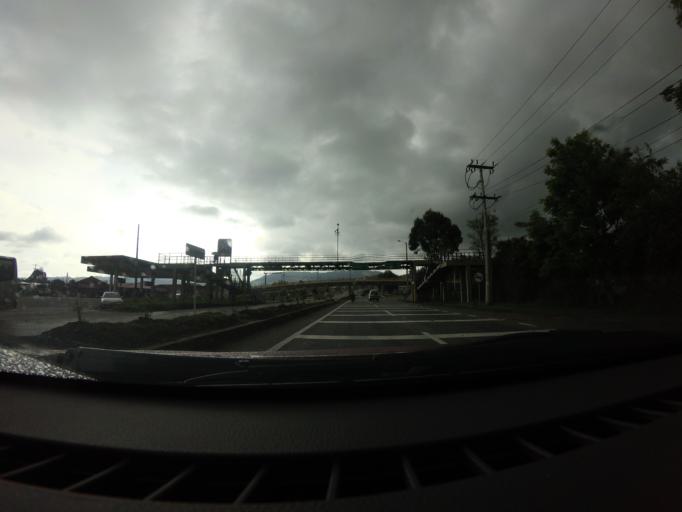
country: CO
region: Cundinamarca
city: El Rosal
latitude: 4.8503
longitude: -74.2730
